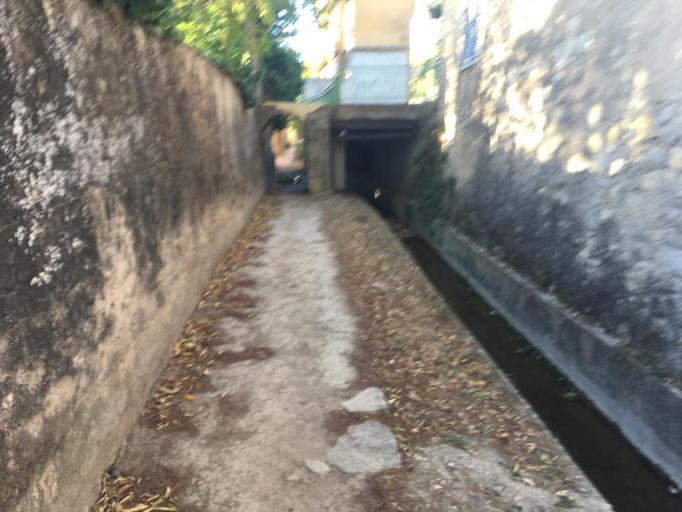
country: FR
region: Provence-Alpes-Cote d'Azur
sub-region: Departement du Var
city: Draguignan
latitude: 43.5435
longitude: 6.4612
